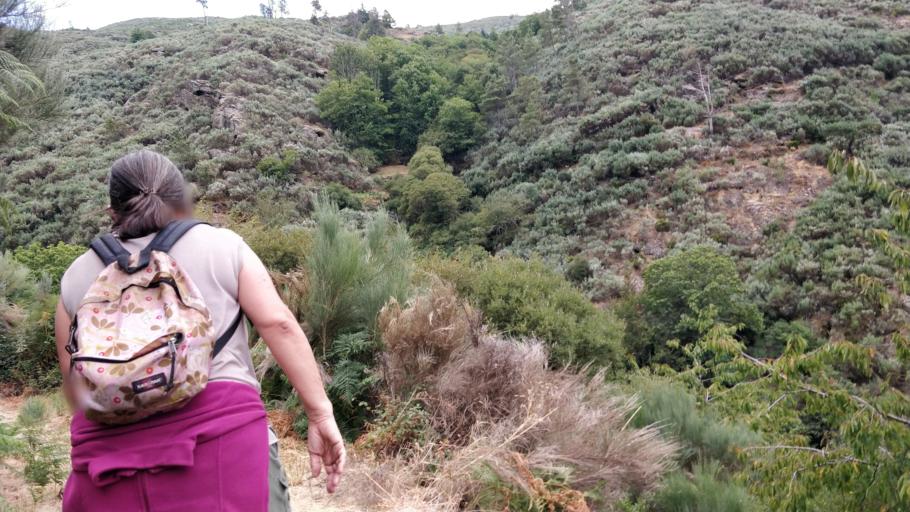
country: PT
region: Guarda
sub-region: Seia
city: Seia
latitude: 40.3795
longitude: -7.6878
